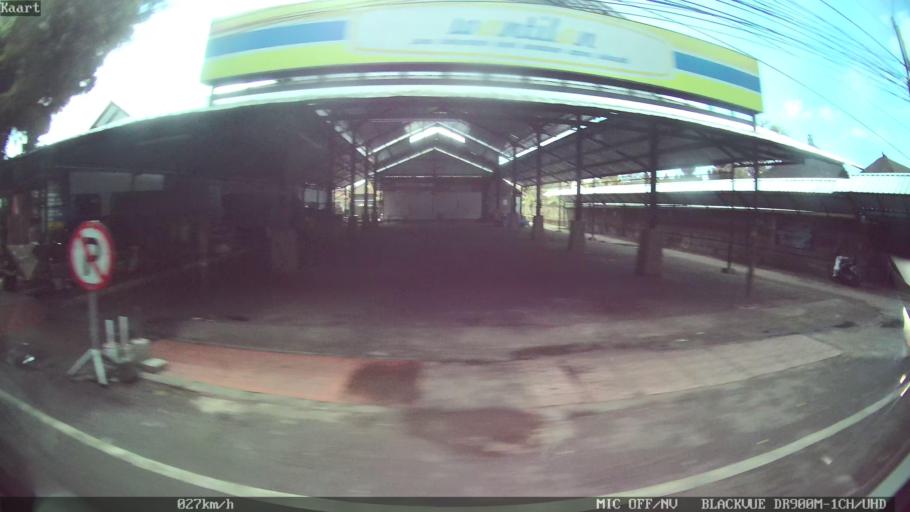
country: ID
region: Bali
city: Banjar Pasekan
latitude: -8.5926
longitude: 115.2827
